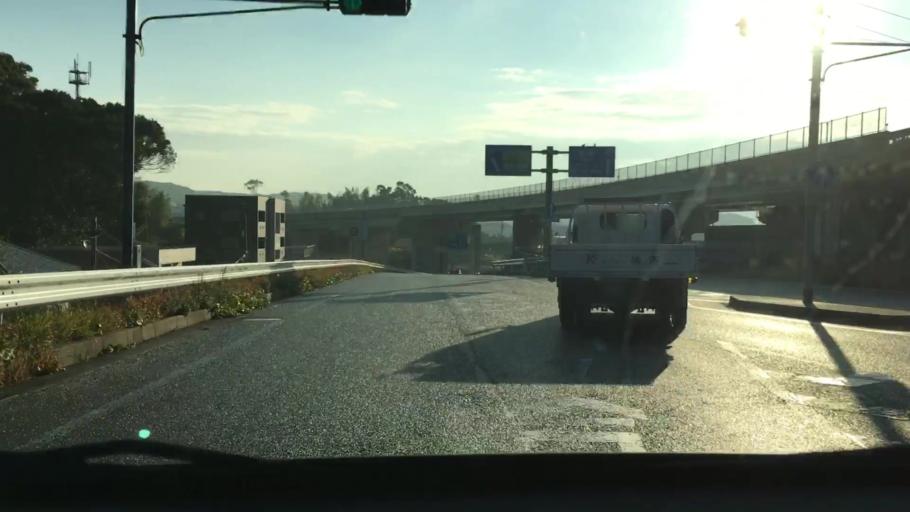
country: JP
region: Nagasaki
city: Sasebo
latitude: 33.1473
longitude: 129.7759
